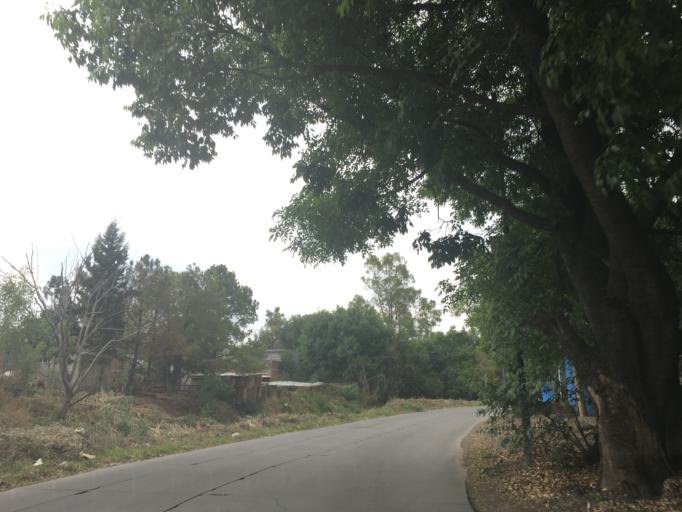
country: MX
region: Michoacan
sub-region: Morelia
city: Morelos
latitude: 19.6707
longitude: -101.2355
